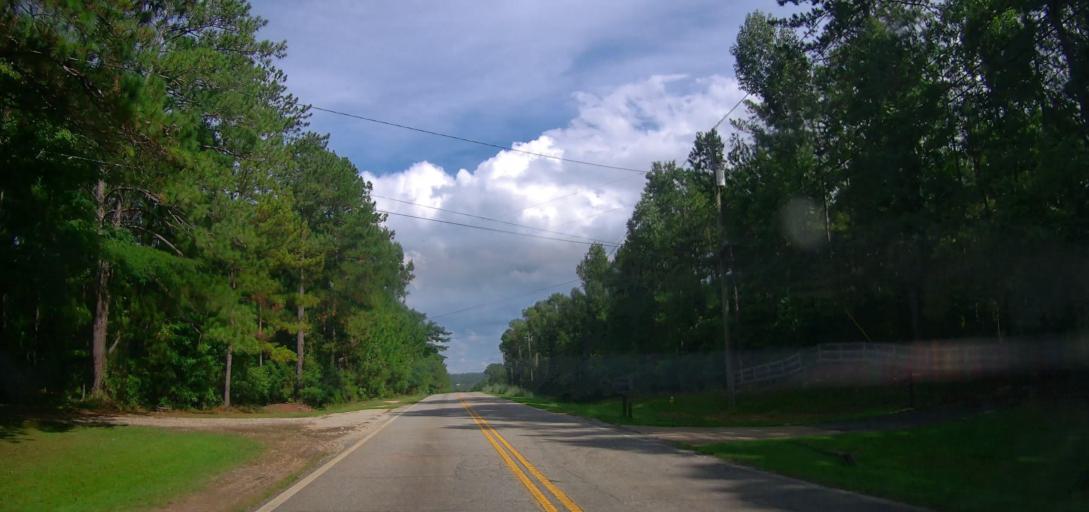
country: US
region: Alabama
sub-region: Russell County
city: Phenix City
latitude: 32.6072
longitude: -84.9638
